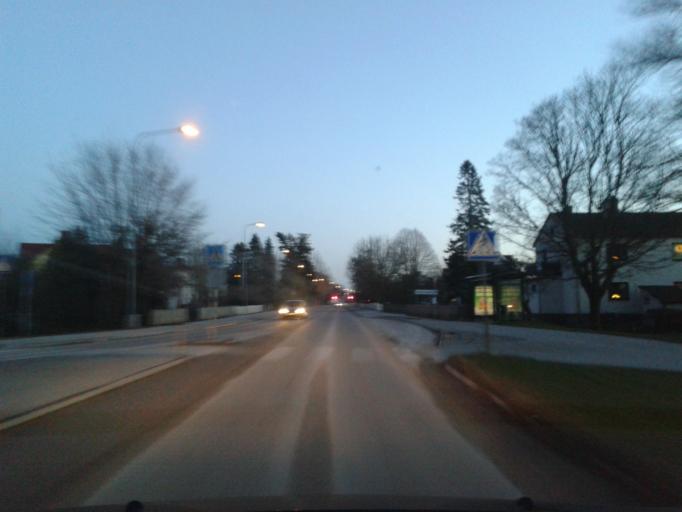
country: SE
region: Gotland
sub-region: Gotland
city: Visby
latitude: 57.6345
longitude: 18.3079
